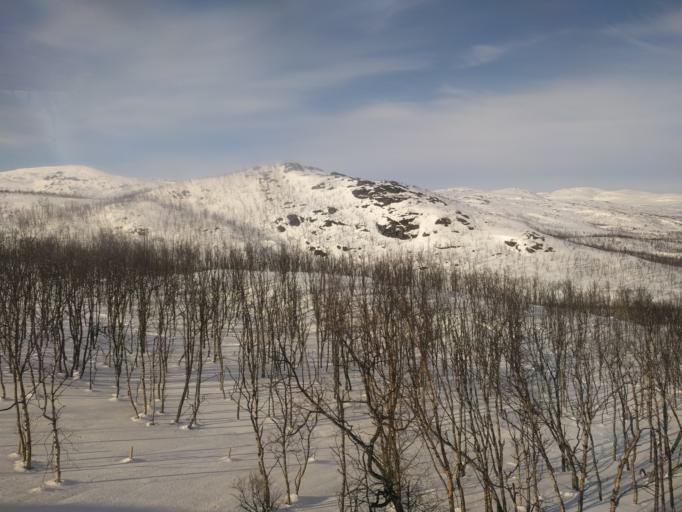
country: NO
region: Troms
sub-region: Bardu
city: Setermoen
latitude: 68.4254
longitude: 18.4346
